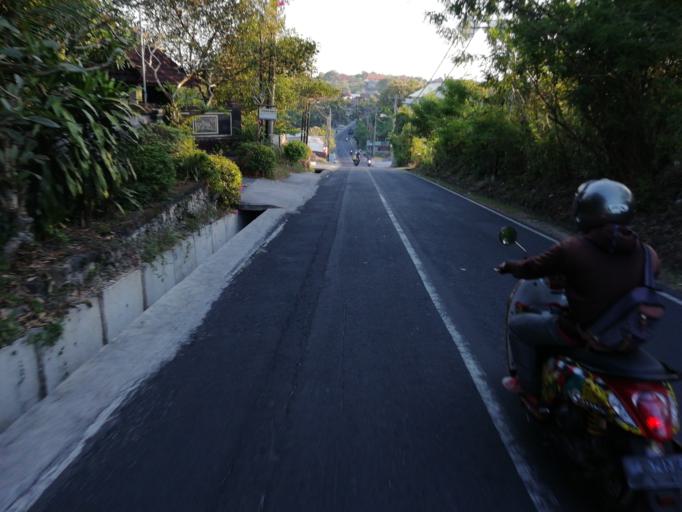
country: ID
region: Bali
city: Bualu
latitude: -8.8205
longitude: 115.1888
